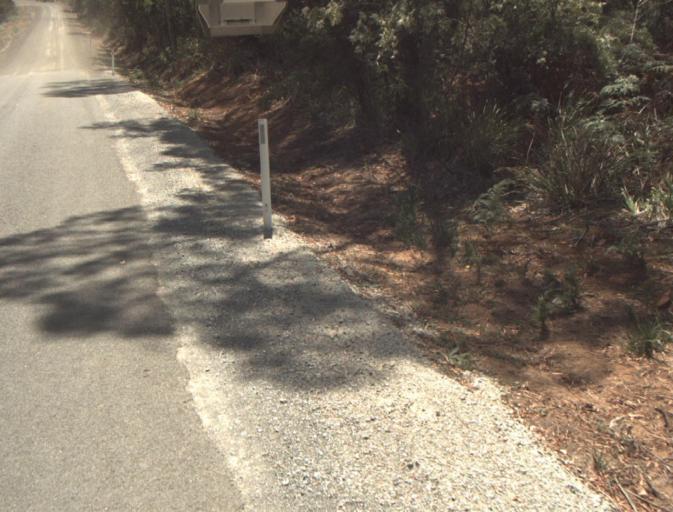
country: AU
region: Tasmania
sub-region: Launceston
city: Mayfield
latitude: -41.2803
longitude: 147.1182
